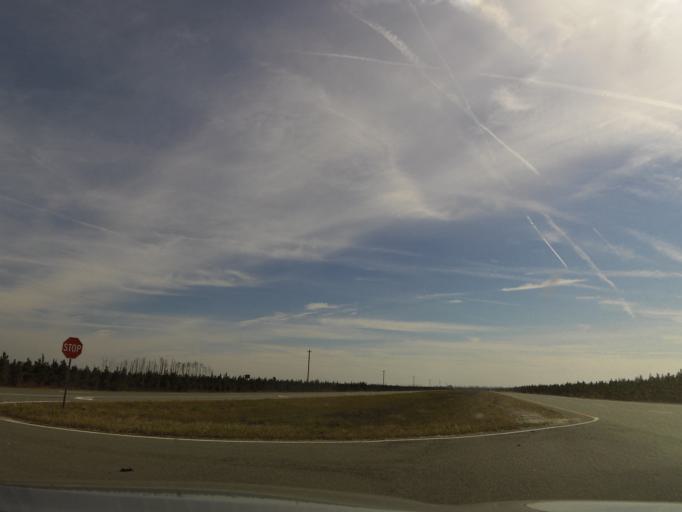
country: US
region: Georgia
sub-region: Ware County
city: Waycross
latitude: 31.0544
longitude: -82.1728
